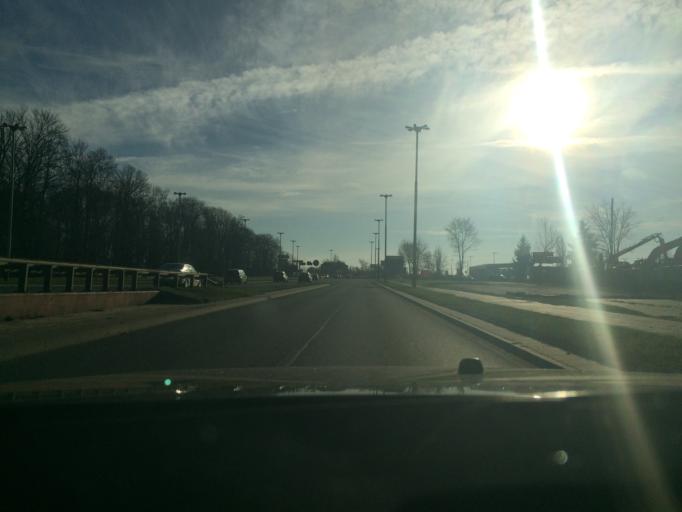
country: PL
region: Lodz Voivodeship
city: Lodz
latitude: 51.7543
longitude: 19.4353
